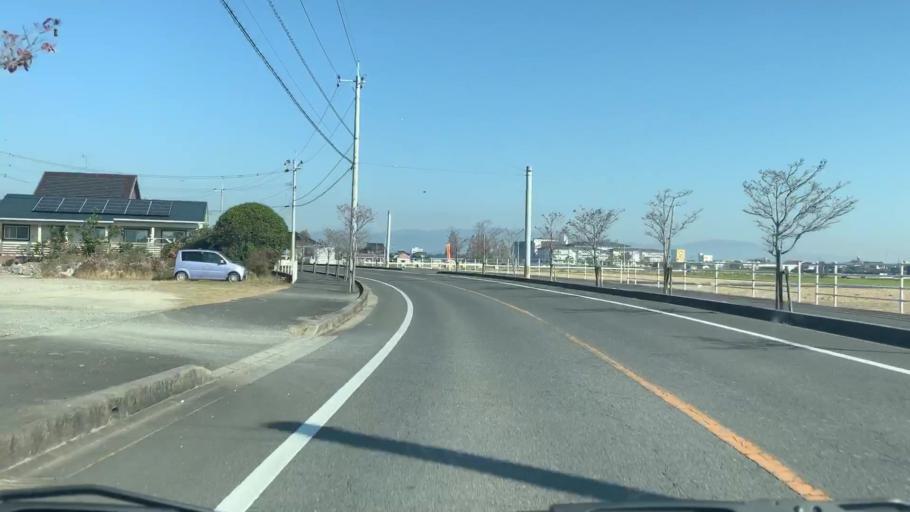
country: JP
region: Saga Prefecture
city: Saga-shi
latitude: 33.2334
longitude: 130.3128
